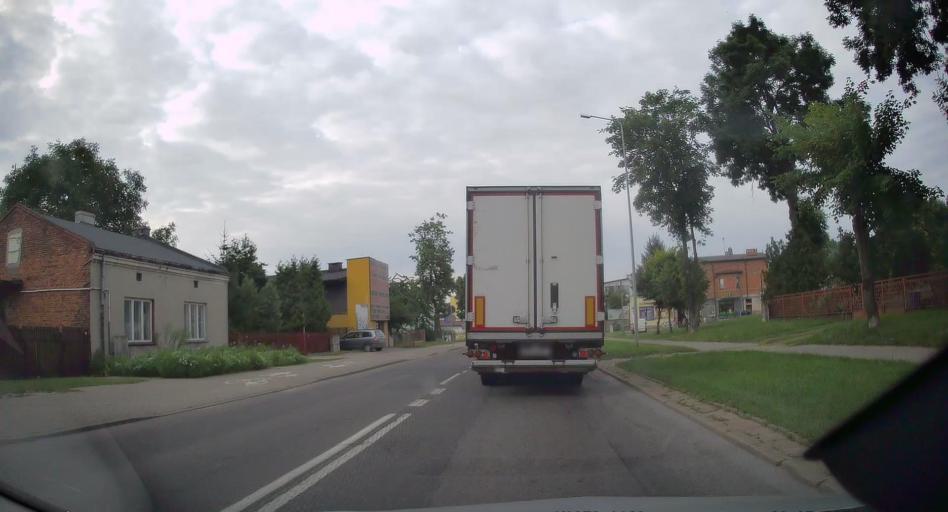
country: PL
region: Lodz Voivodeship
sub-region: Powiat radomszczanski
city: Radomsko
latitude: 51.0605
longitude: 19.4417
